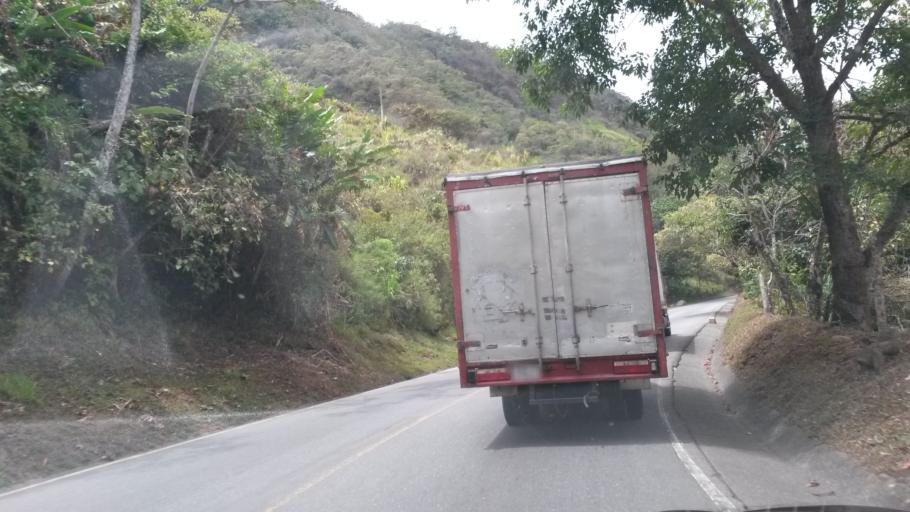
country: CO
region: Cauca
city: Rosas
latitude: 2.2613
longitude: -76.7472
